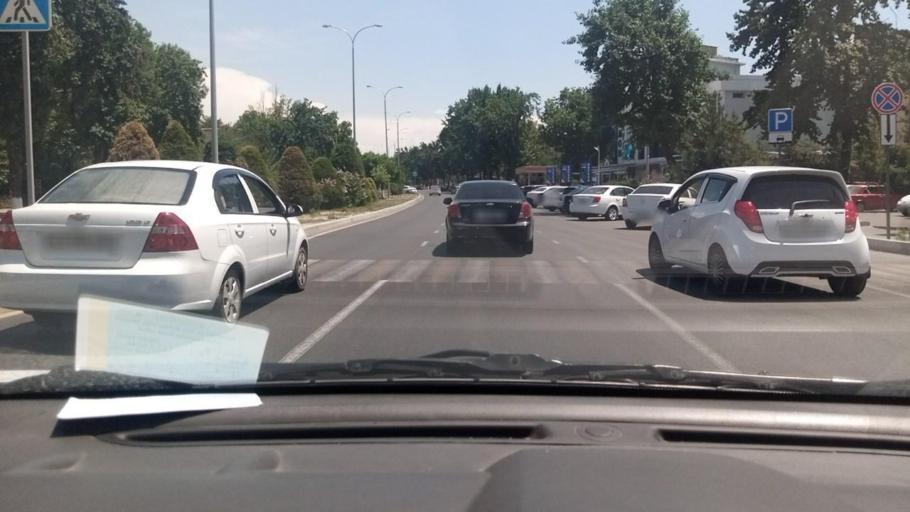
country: UZ
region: Toshkent Shahri
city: Tashkent
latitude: 41.2891
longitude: 69.2017
